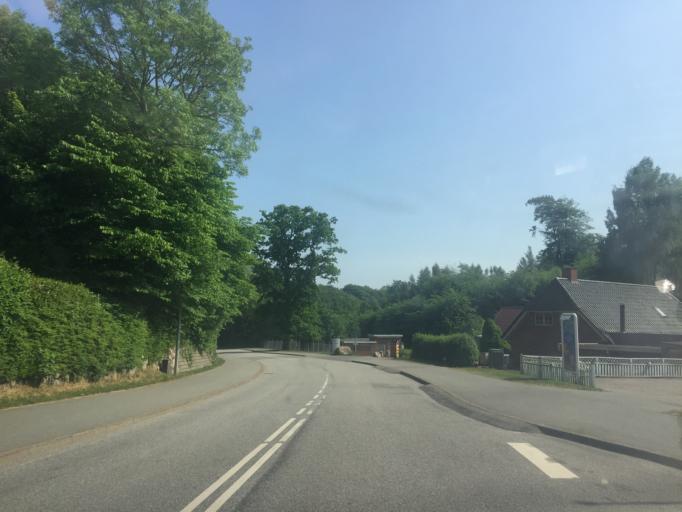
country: DK
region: South Denmark
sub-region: Kolding Kommune
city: Kolding
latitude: 55.4776
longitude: 9.5069
